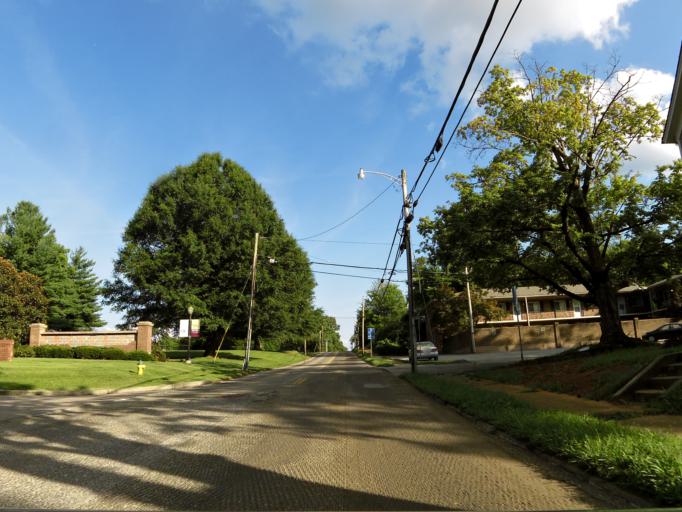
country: US
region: Tennessee
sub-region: Blount County
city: Maryville
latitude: 35.7504
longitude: -83.9661
